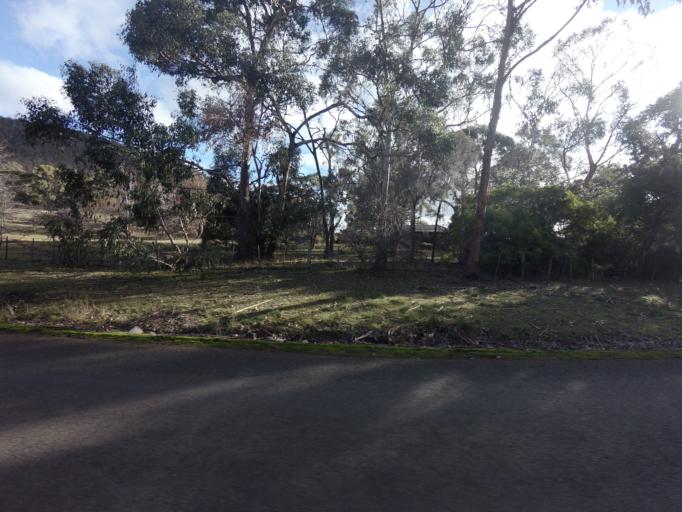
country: AU
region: Tasmania
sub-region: Derwent Valley
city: New Norfolk
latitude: -42.7920
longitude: 147.1226
